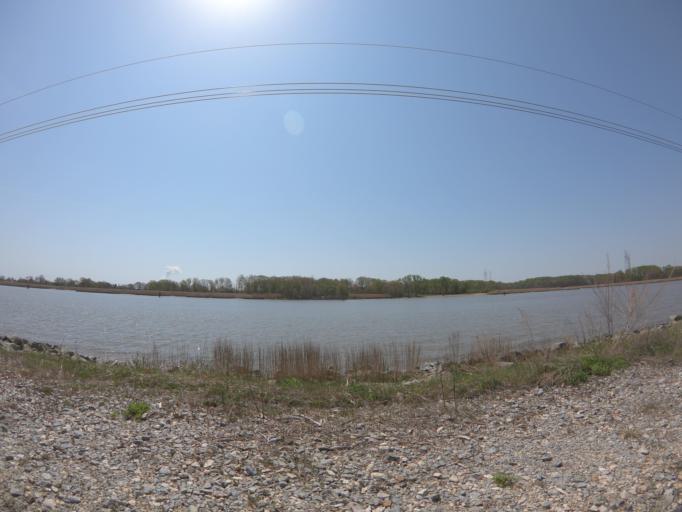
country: US
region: Delaware
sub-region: New Castle County
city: Delaware City
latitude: 39.5554
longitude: -75.6144
